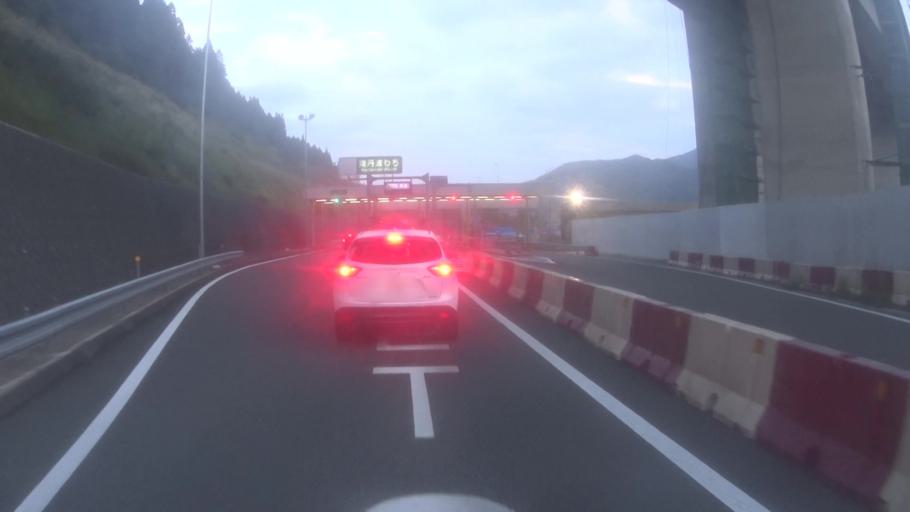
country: JP
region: Kyoto
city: Ayabe
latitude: 35.2774
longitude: 135.3378
